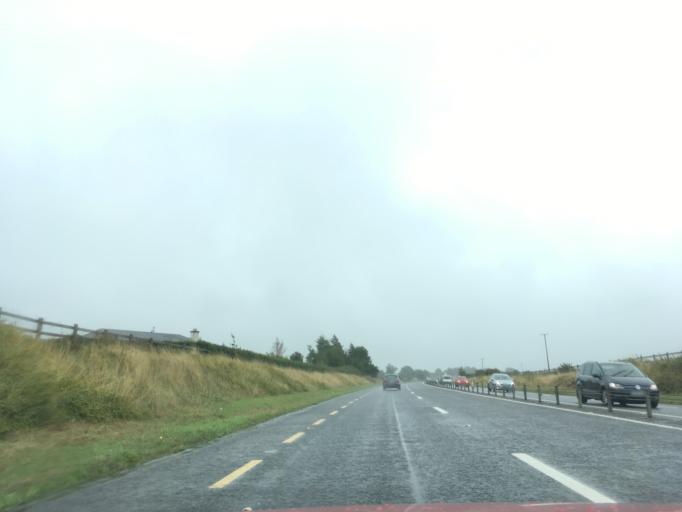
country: IE
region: Leinster
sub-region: Kilkenny
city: Piltown
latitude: 52.3557
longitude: -7.3660
